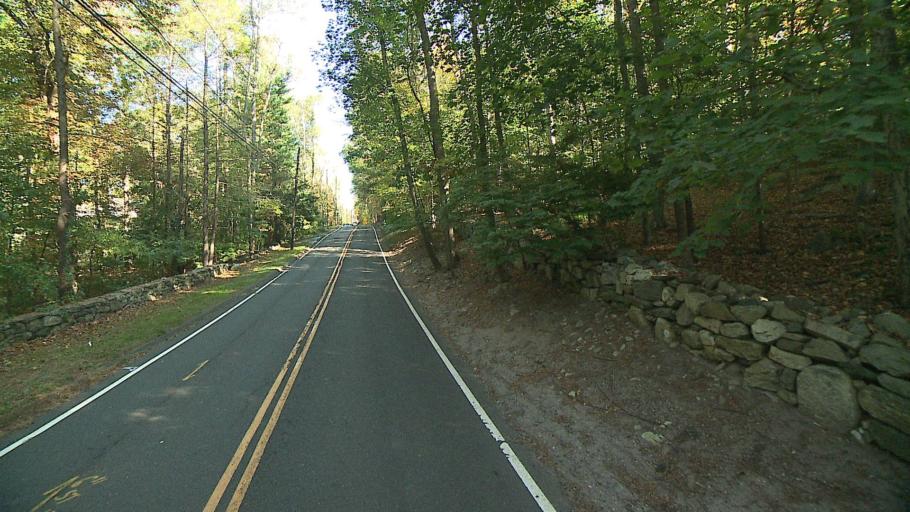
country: US
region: Connecticut
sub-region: Fairfield County
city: Westport
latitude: 41.1913
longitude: -73.3386
